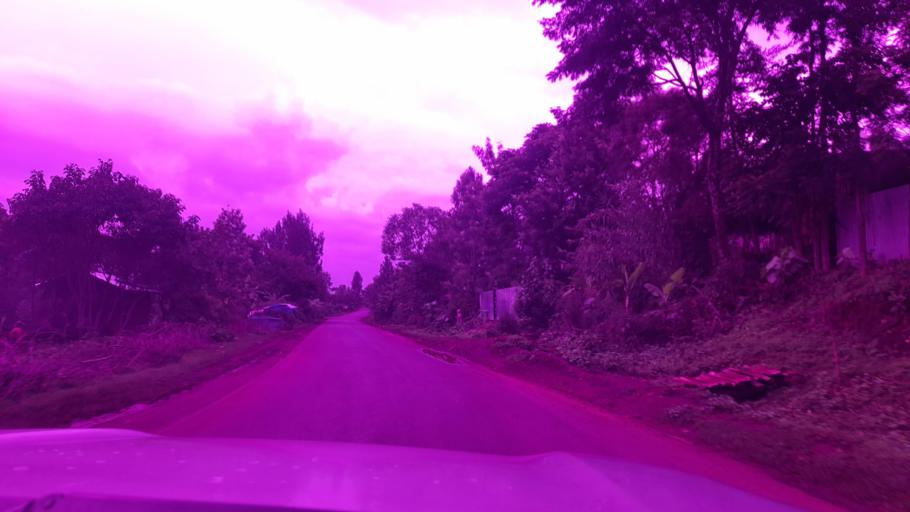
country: ET
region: Oromiya
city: Jima
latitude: 7.8962
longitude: 37.3896
